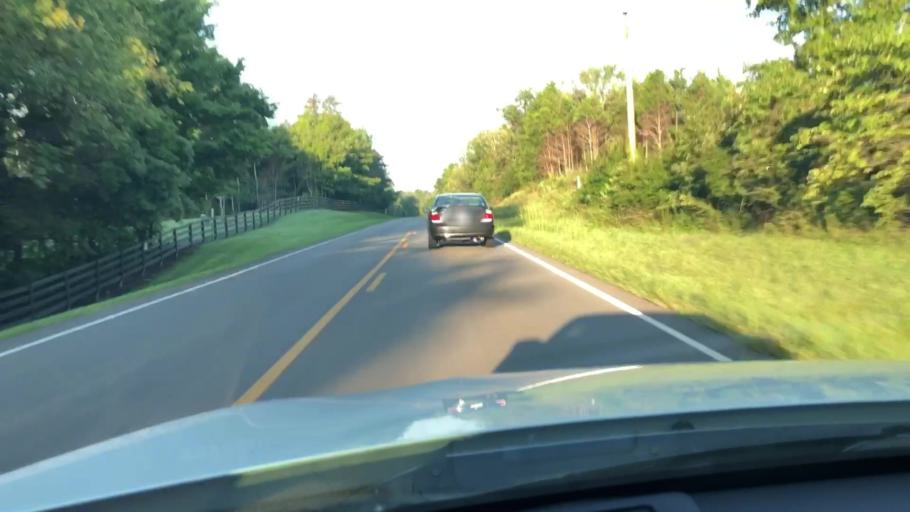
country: US
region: Kentucky
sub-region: Jefferson County
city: Middletown
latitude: 38.2211
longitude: -85.5117
